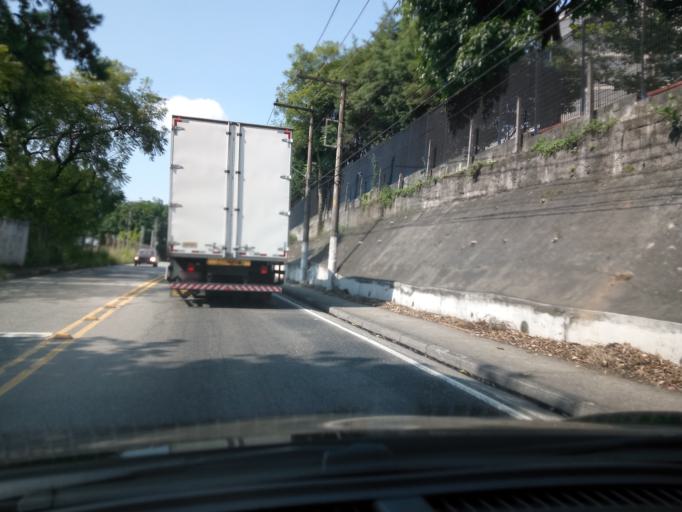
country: BR
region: Sao Paulo
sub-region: Sao Caetano Do Sul
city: Sao Caetano do Sul
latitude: -23.6503
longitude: -46.5832
